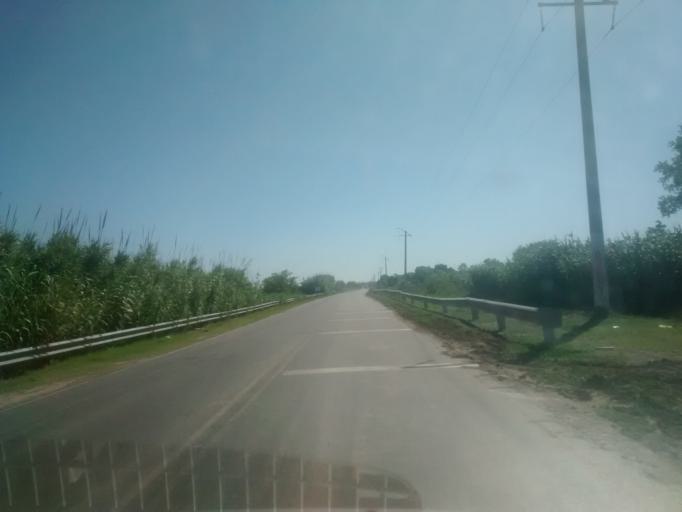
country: AR
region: Buenos Aires
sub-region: Partido de Berisso
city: Berisso
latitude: -34.8860
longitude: -57.8599
